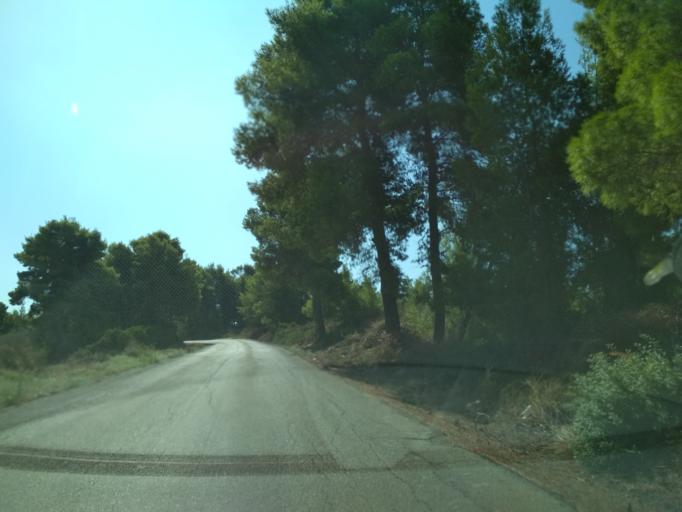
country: GR
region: Central Greece
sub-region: Nomos Evvoias
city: Roviai
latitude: 38.8220
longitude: 23.2316
